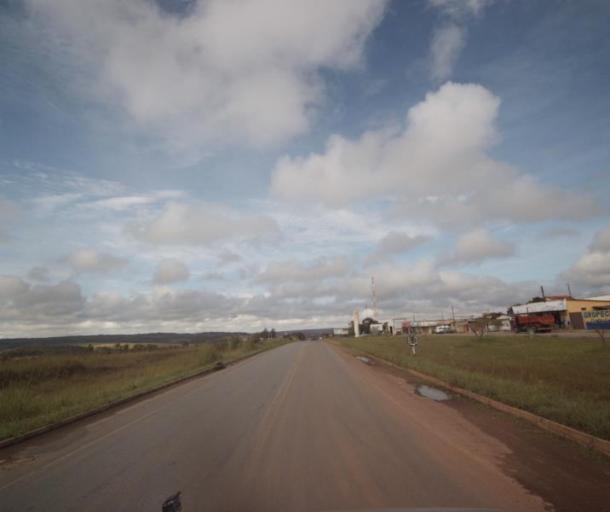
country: BR
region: Goias
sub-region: Pirenopolis
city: Pirenopolis
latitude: -15.7759
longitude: -48.7645
